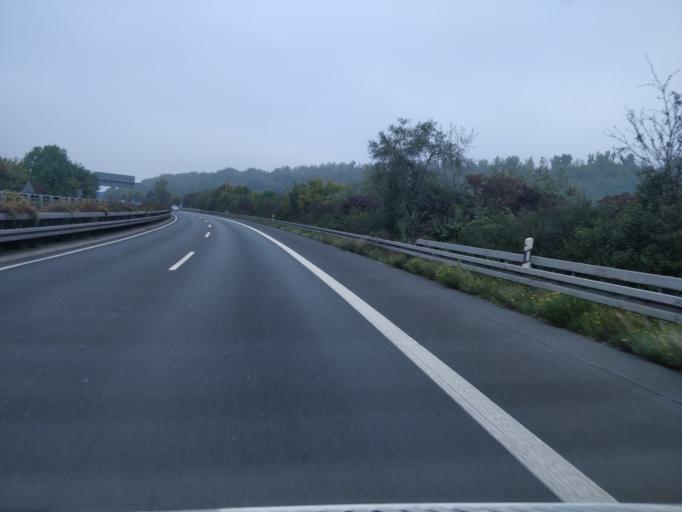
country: DE
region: North Rhine-Westphalia
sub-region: Regierungsbezirk Dusseldorf
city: Dinslaken
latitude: 51.5331
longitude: 6.7563
